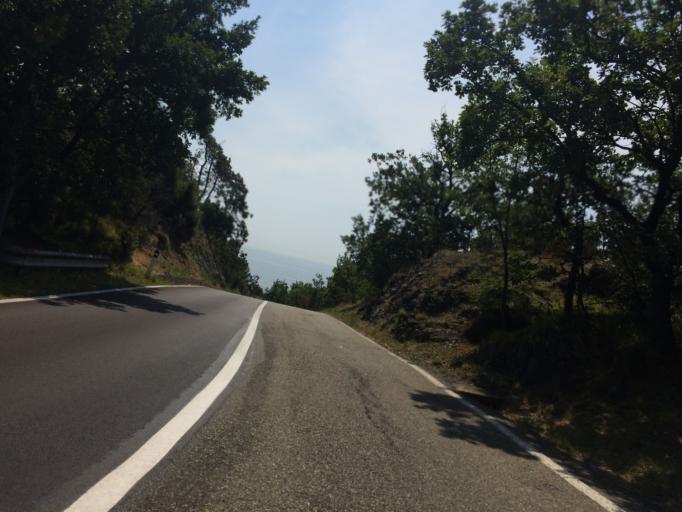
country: IT
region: Liguria
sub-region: Provincia di Genova
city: Cogoleto
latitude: 44.3881
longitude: 8.6338
